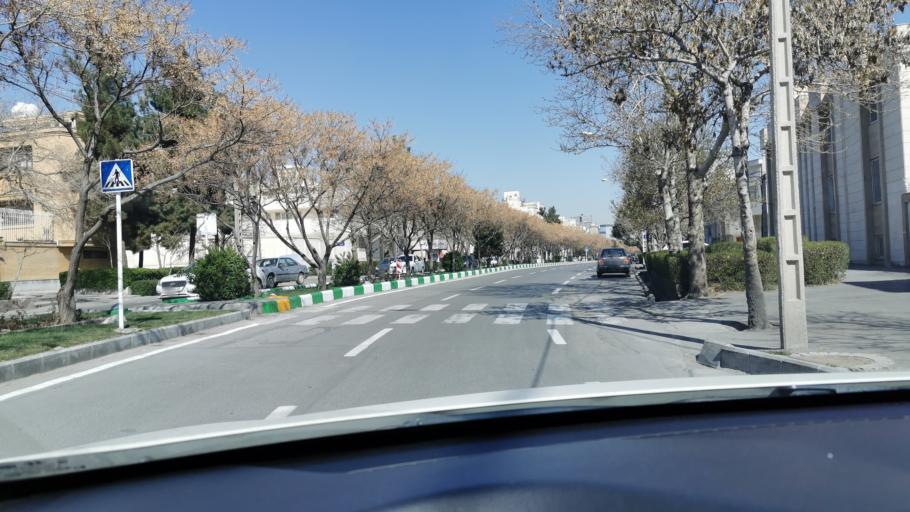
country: IR
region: Razavi Khorasan
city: Mashhad
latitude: 36.2893
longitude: 59.5726
